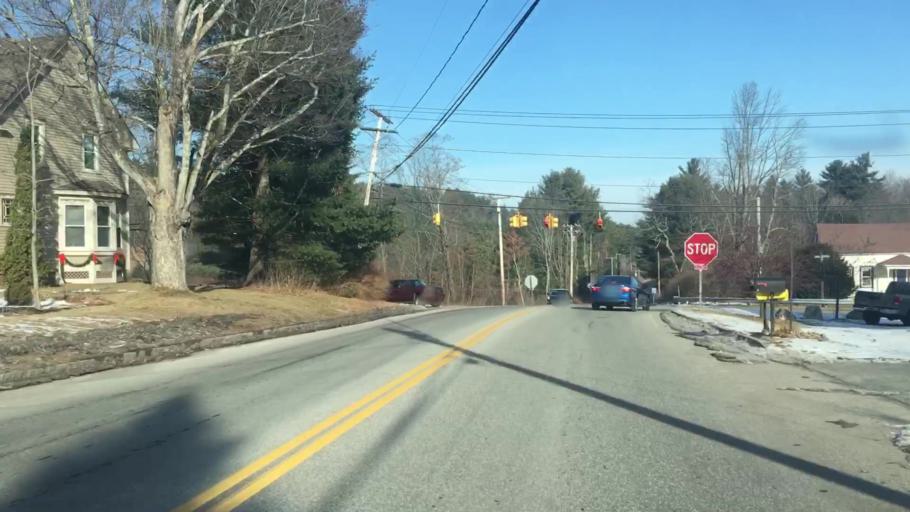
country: US
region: Maine
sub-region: Androscoggin County
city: Auburn
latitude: 44.1266
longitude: -70.2714
